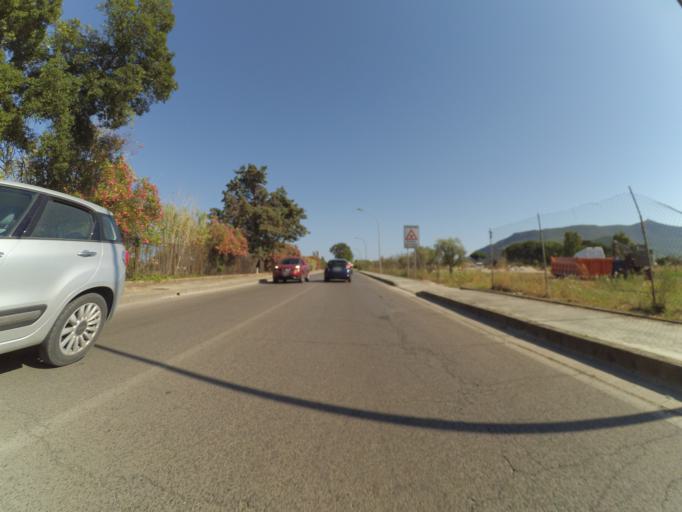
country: IT
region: Latium
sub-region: Provincia di Latina
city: San Felice Circeo
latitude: 41.2550
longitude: 13.0929
